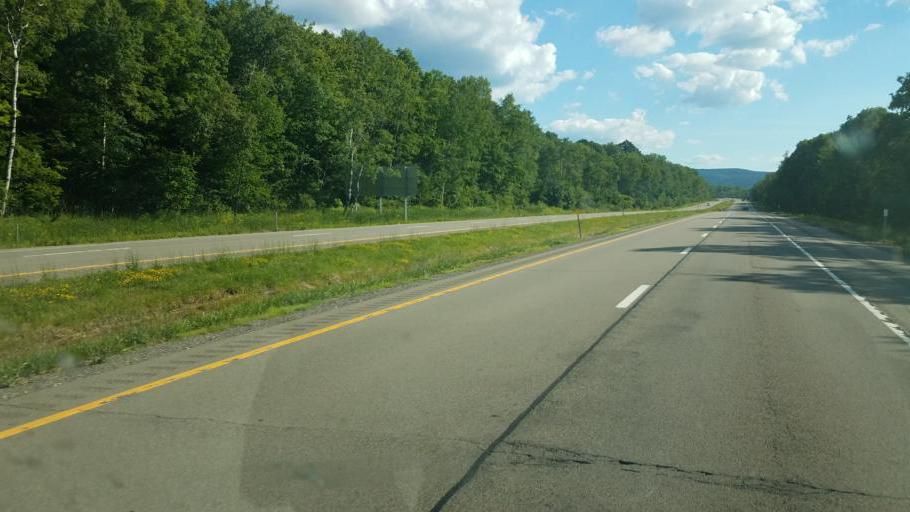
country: US
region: New York
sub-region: Cattaraugus County
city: Salamanca
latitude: 42.1439
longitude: -78.7703
